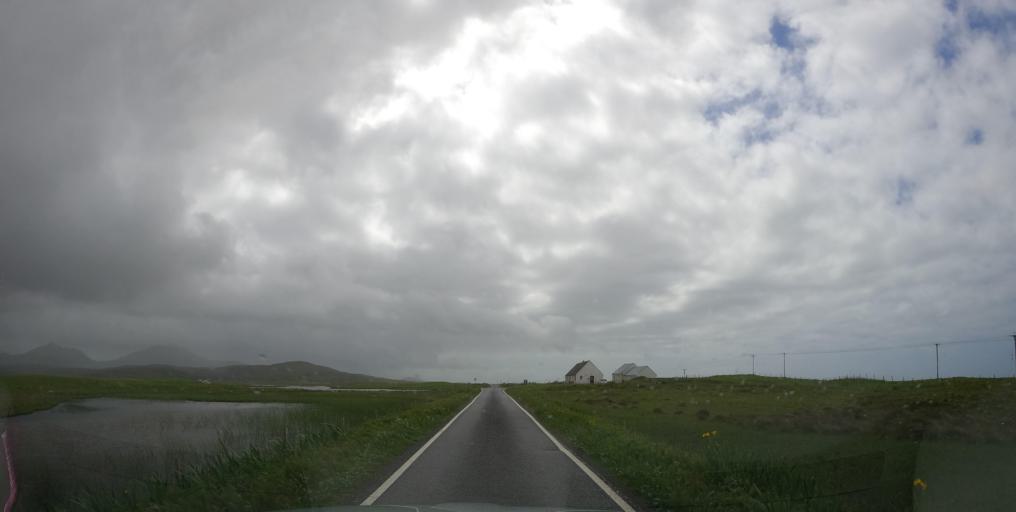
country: GB
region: Scotland
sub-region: Eilean Siar
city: Isle of South Uist
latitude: 57.3222
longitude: -7.3683
